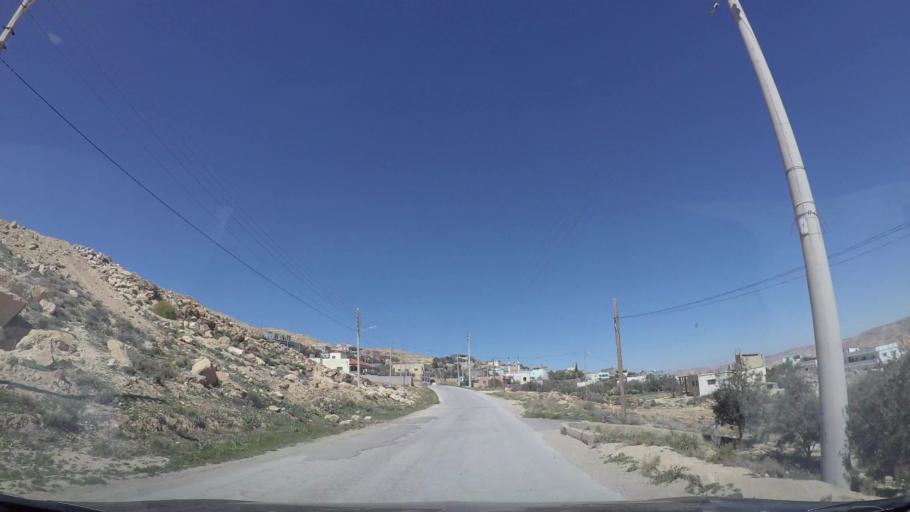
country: JO
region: Tafielah
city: At Tafilah
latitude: 30.8337
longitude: 35.5761
